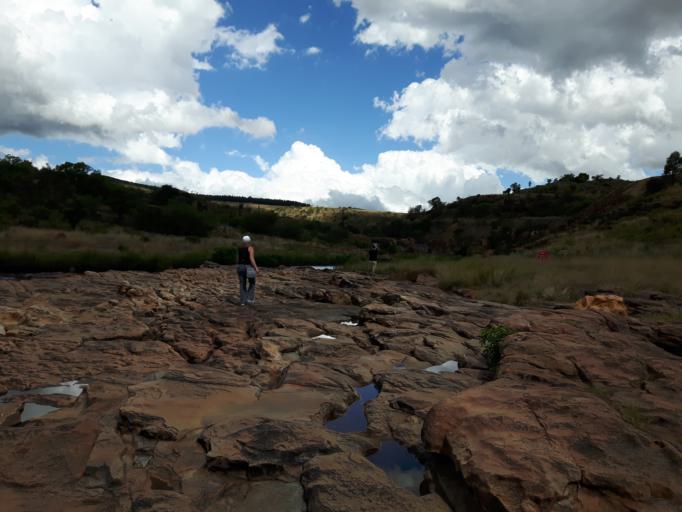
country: ZA
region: Mpumalanga
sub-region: Ehlanzeni District
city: Graksop
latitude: -24.6752
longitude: 30.8113
